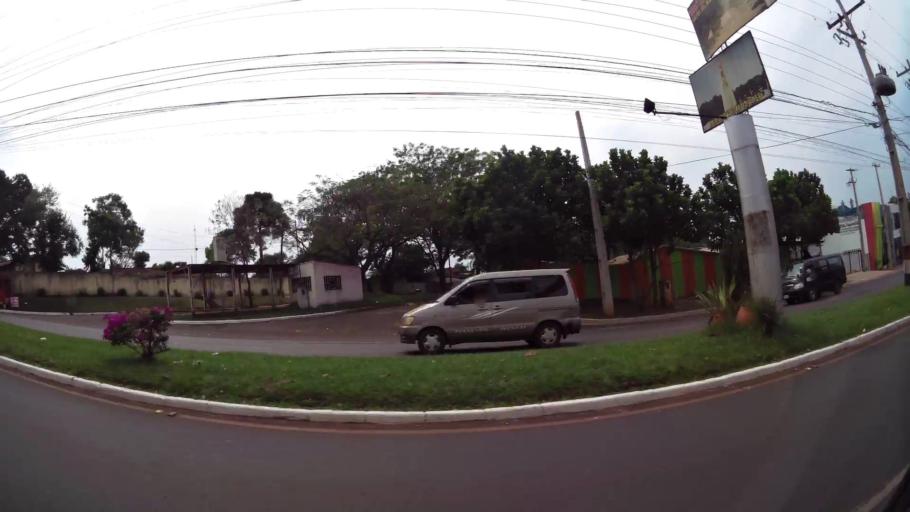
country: PY
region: Alto Parana
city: Presidente Franco
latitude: -25.5422
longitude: -54.6334
